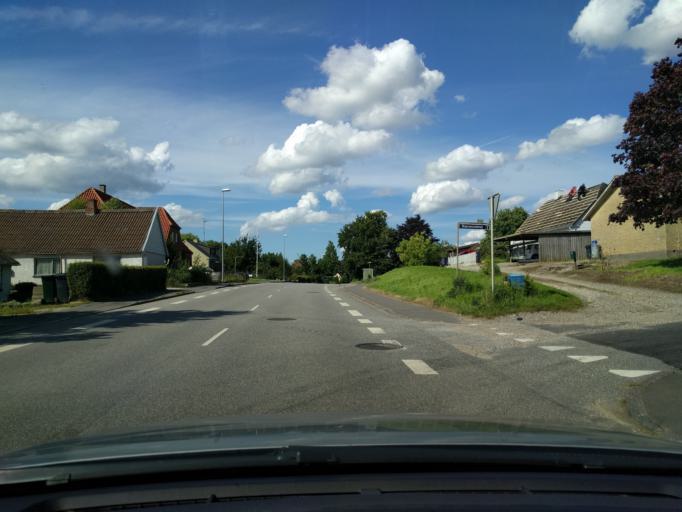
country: DK
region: Zealand
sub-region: Guldborgsund Kommune
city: Stubbekobing
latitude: 54.8631
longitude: 12.0195
